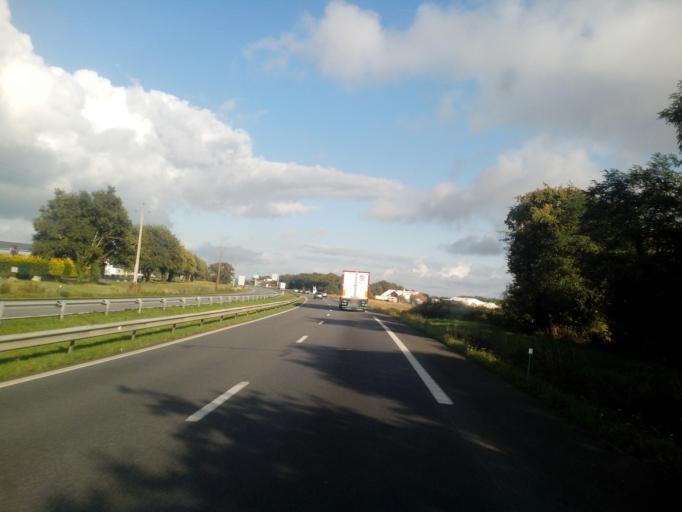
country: FR
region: Brittany
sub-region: Departement du Morbihan
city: Peaule
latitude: 47.5363
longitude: -2.4066
